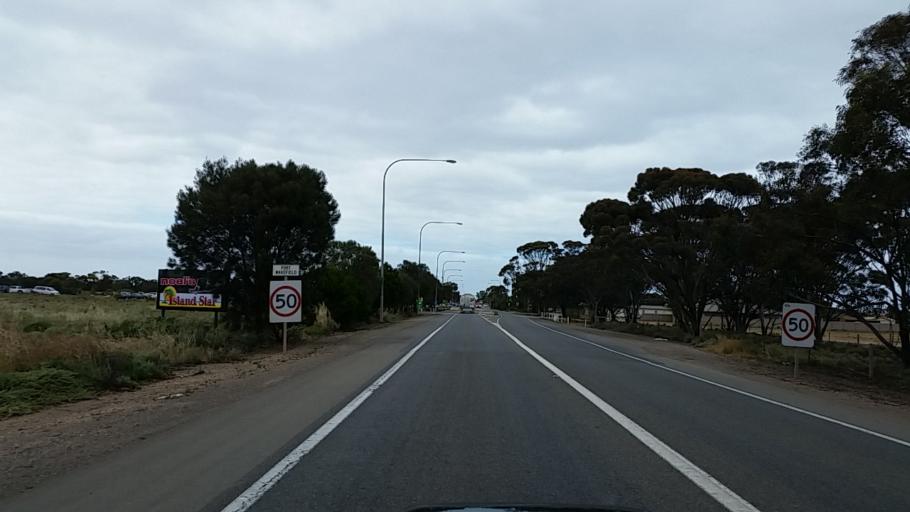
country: AU
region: South Australia
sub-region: Wakefield
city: Balaklava
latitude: -34.1787
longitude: 138.1541
